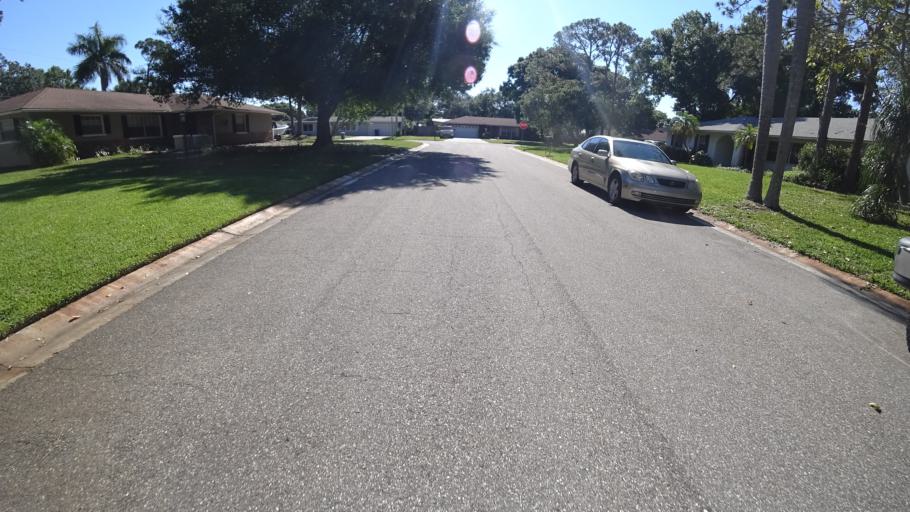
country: US
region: Florida
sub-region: Manatee County
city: West Bradenton
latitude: 27.4829
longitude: -82.6106
